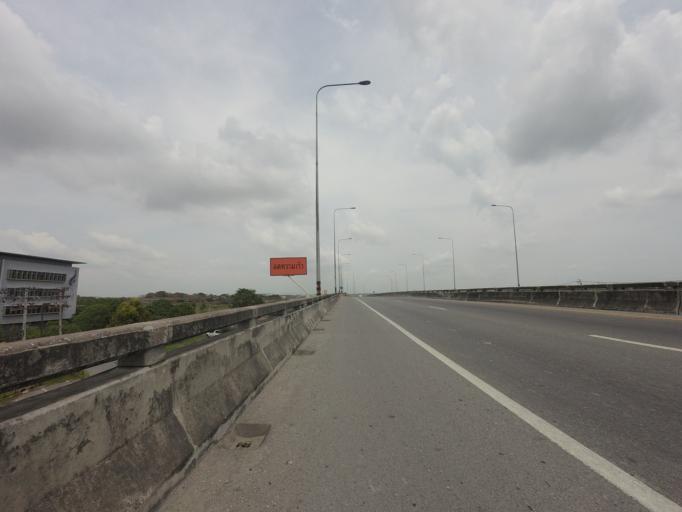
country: TH
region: Bangkok
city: Lat Krabang
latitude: 13.6472
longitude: 100.7459
